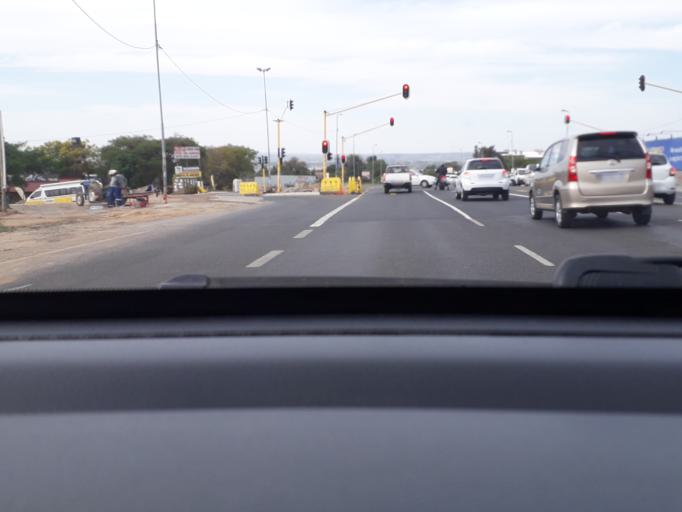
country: ZA
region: Gauteng
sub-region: West Rand District Municipality
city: Muldersdriseloop
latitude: -26.0549
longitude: 27.9467
